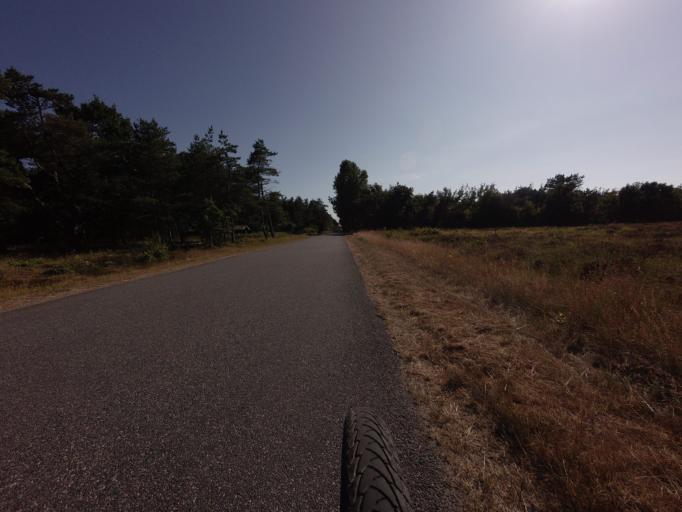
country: DK
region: North Denmark
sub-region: Laeso Kommune
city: Byrum
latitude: 57.2740
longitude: 10.9051
